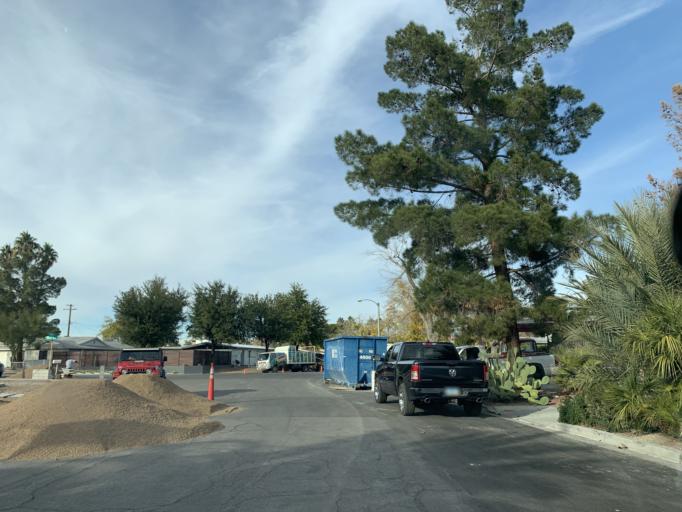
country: US
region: Nevada
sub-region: Clark County
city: Las Vegas
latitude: 36.1503
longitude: -115.1692
